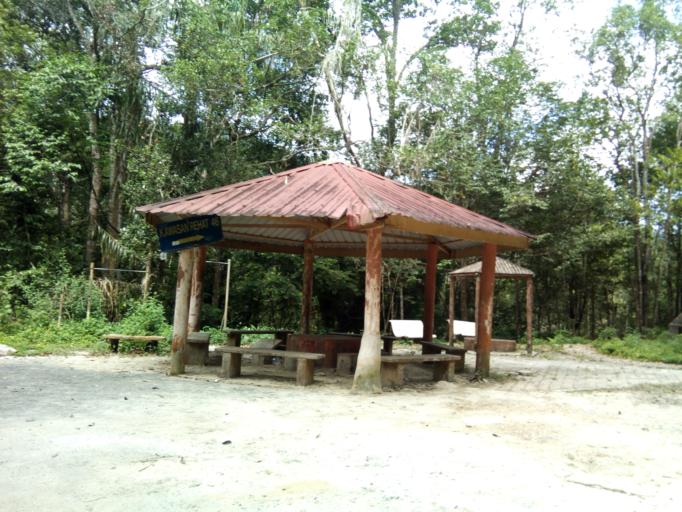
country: MY
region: Penang
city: Tanjung Tokong
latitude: 5.4362
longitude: 100.2821
